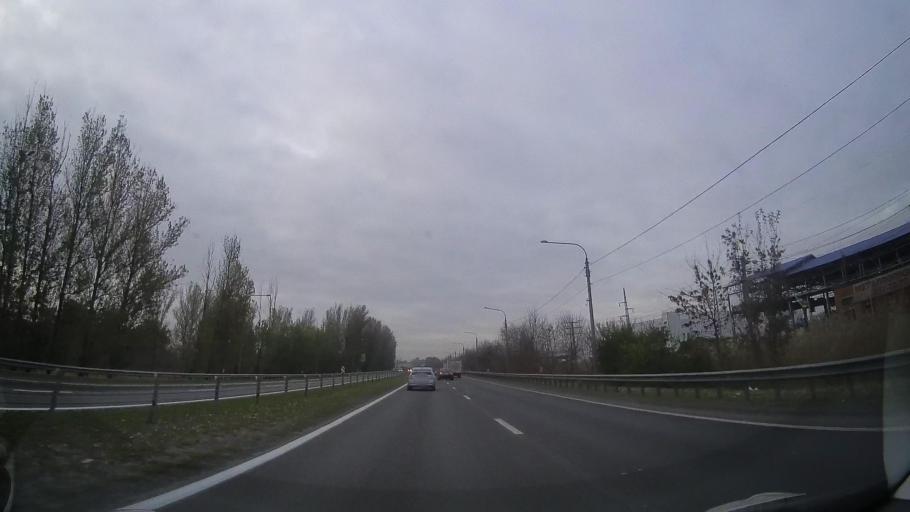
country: RU
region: Rostov
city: Bataysk
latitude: 47.1145
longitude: 39.7680
